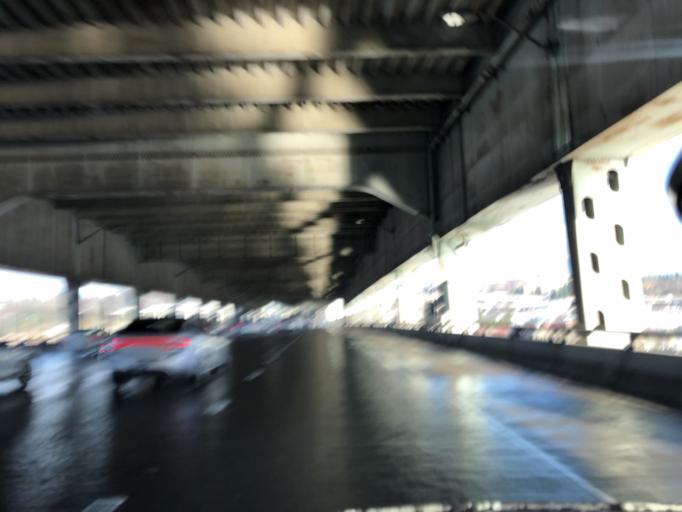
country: US
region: Oregon
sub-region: Multnomah County
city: Portland
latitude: 45.5388
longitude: -122.6817
